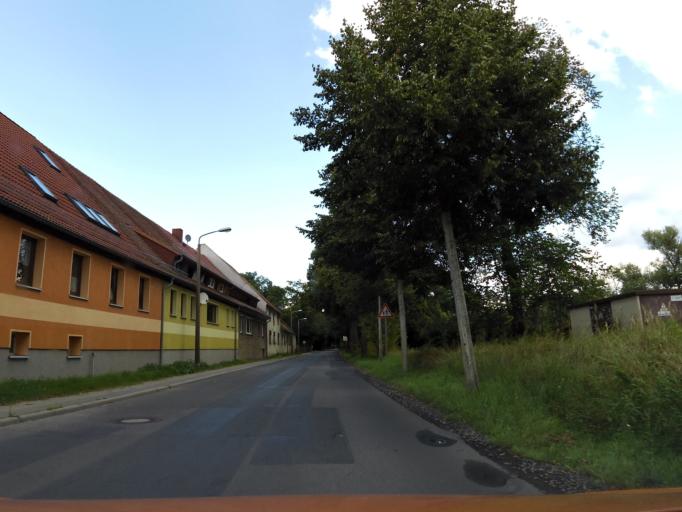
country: DE
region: Brandenburg
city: Potsdam
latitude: 52.4646
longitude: 13.0100
